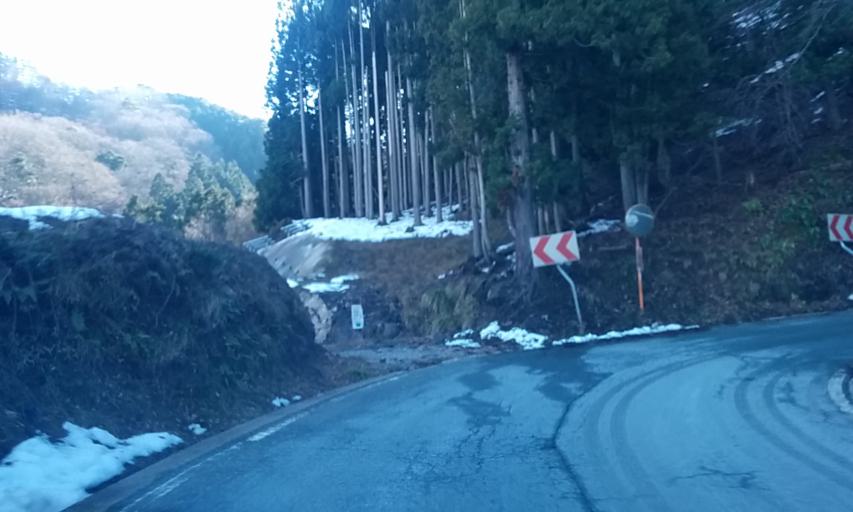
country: JP
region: Hyogo
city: Toyooka
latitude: 35.4121
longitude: 134.9561
